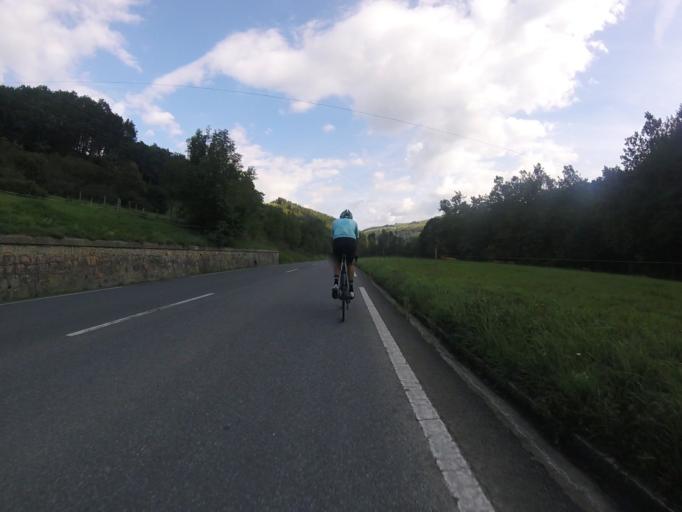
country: ES
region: Basque Country
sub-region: Provincia de Guipuzcoa
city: Amezqueta
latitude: 43.0589
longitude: -2.0878
